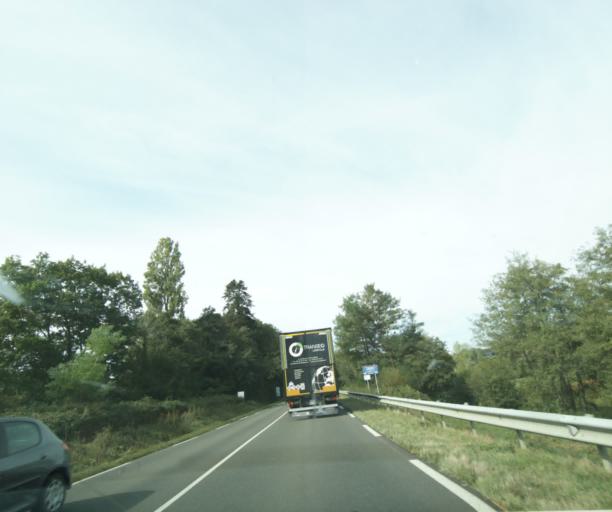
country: FR
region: Auvergne
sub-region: Departement de l'Allier
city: Le Donjon
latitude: 46.3512
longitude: 3.8055
